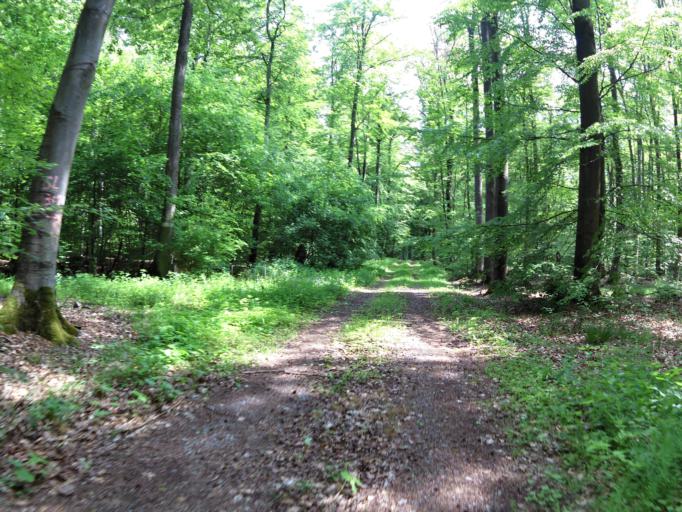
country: DE
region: Bavaria
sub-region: Regierungsbezirk Unterfranken
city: Kist
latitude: 49.7497
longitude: 9.8572
